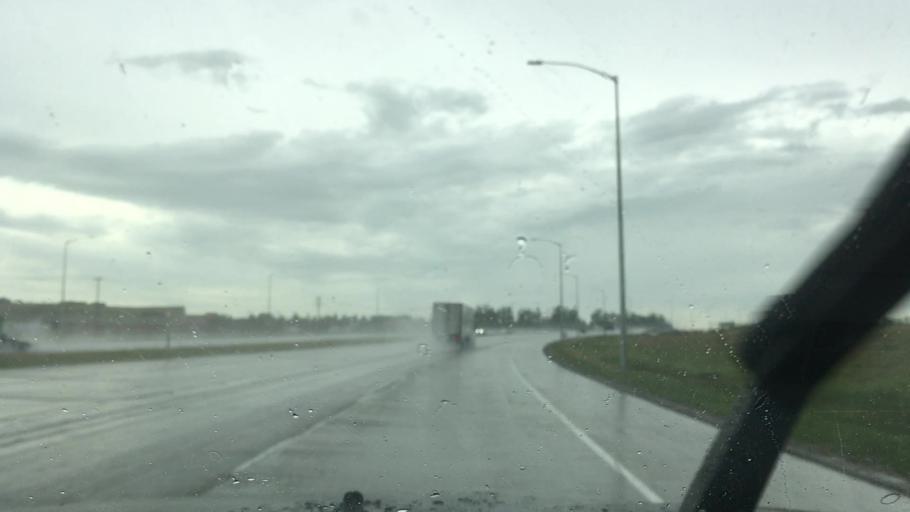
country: CA
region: Alberta
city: Leduc
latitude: 53.2796
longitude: -113.5513
